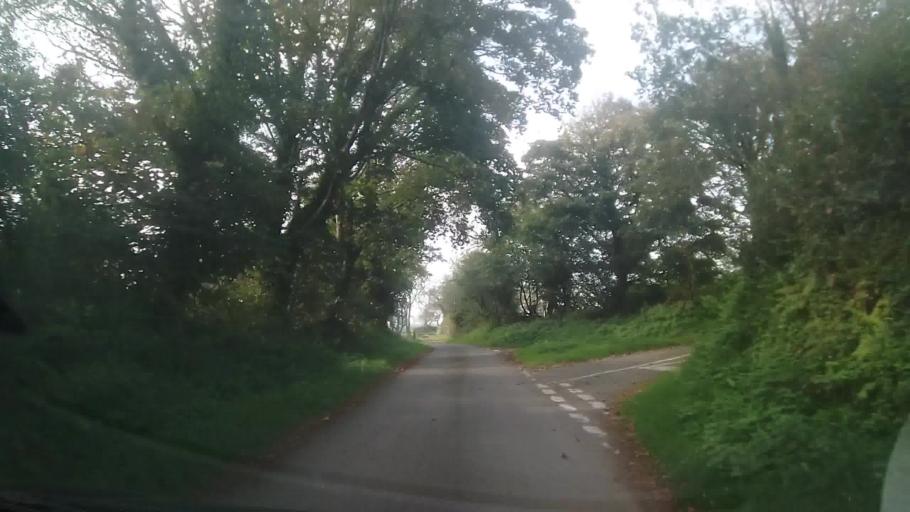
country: GB
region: Wales
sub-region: Pembrokeshire
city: Mathry
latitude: 51.8899
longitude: -5.0584
